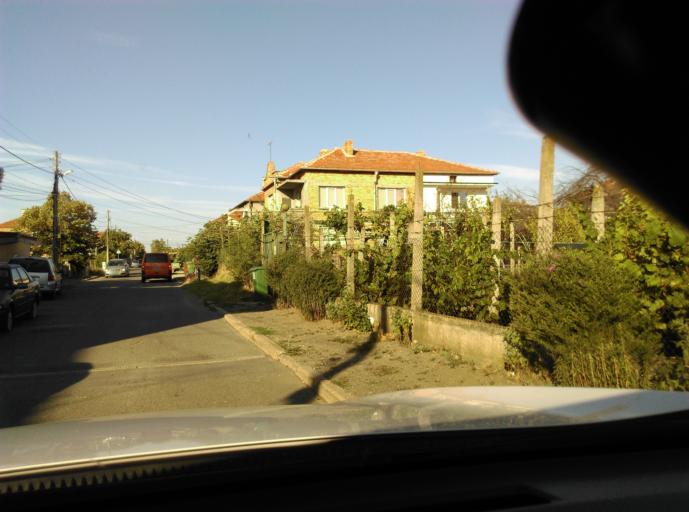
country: BG
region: Burgas
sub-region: Obshtina Kameno
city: Kameno
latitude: 42.6007
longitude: 27.3872
